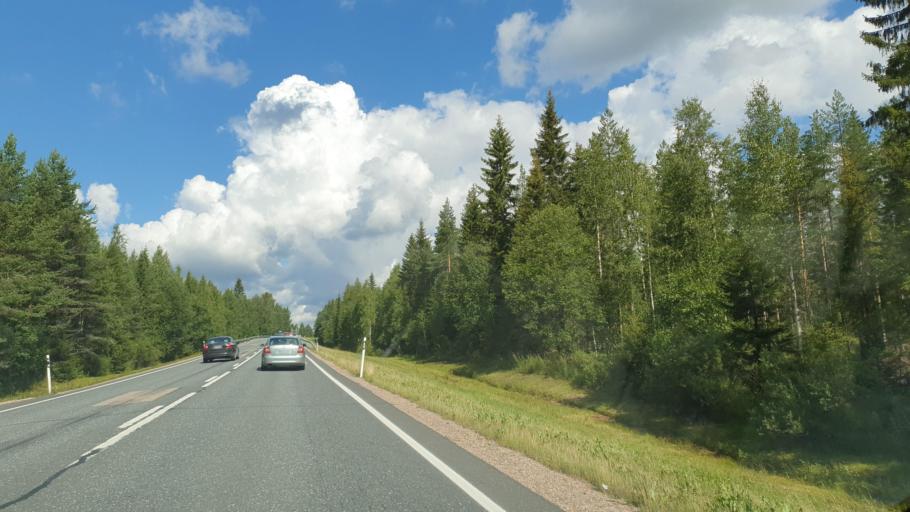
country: FI
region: Kainuu
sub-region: Kajaani
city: Kajaani
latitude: 64.0490
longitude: 27.4516
